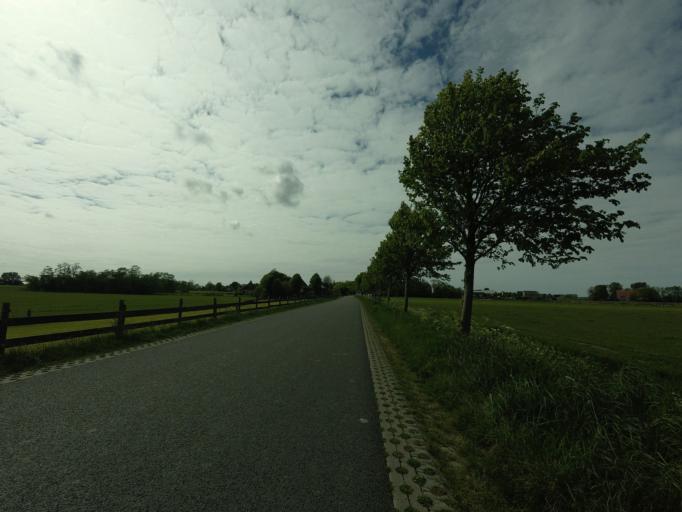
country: NL
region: Friesland
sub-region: Sudwest Fryslan
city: Bolsward
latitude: 53.0199
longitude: 5.5382
